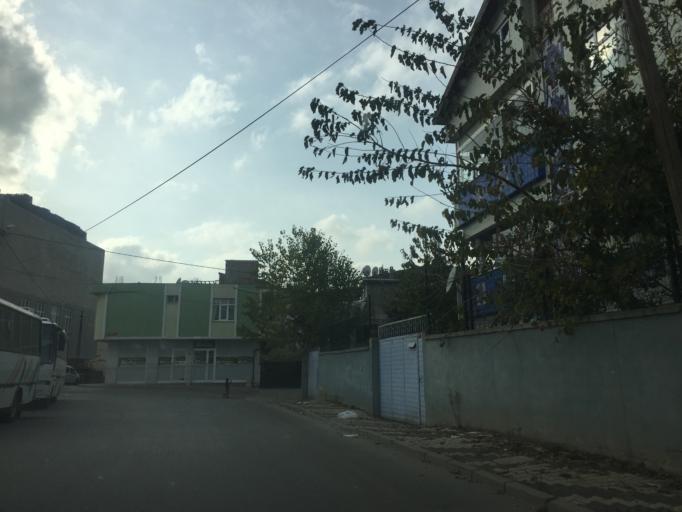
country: TR
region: Istanbul
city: Sultanbeyli
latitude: 40.9377
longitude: 29.2899
